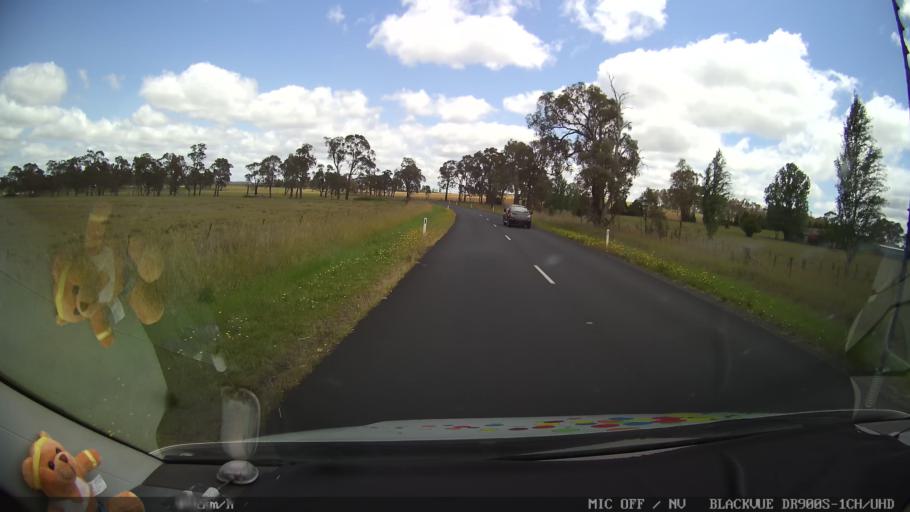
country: AU
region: New South Wales
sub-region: Glen Innes Severn
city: Glen Innes
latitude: -29.6530
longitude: 151.6934
